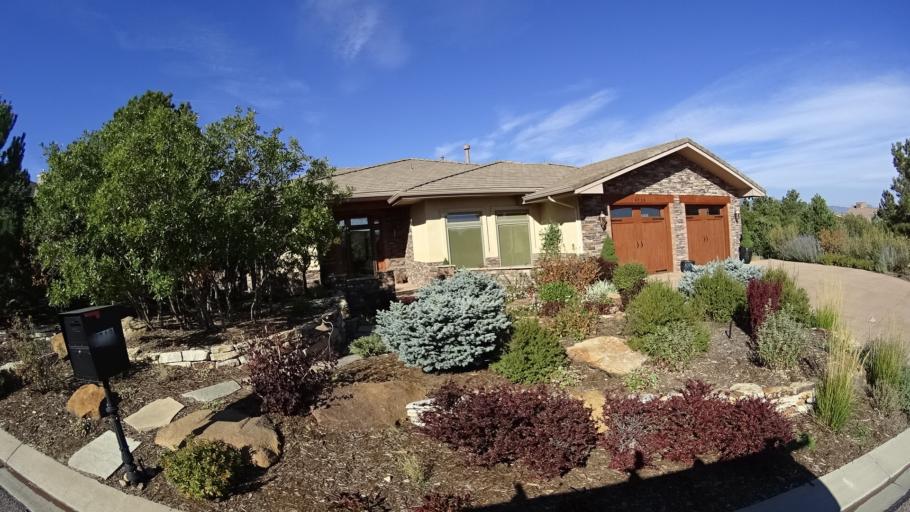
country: US
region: Colorado
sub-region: El Paso County
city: Colorado Springs
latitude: 38.9017
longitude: -104.7962
